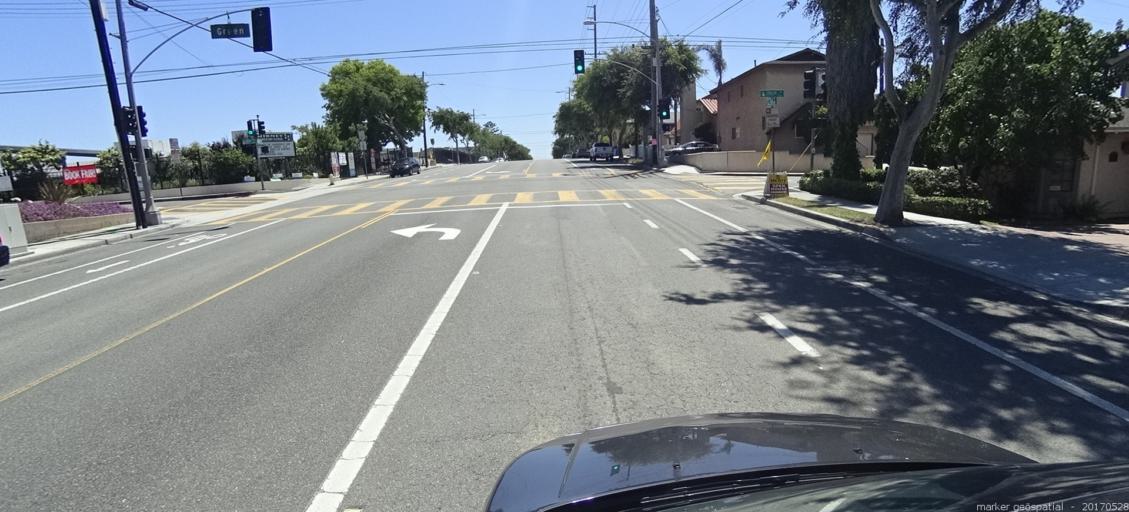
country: US
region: California
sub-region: Los Angeles County
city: Redondo Beach
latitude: 33.8690
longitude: -118.3773
